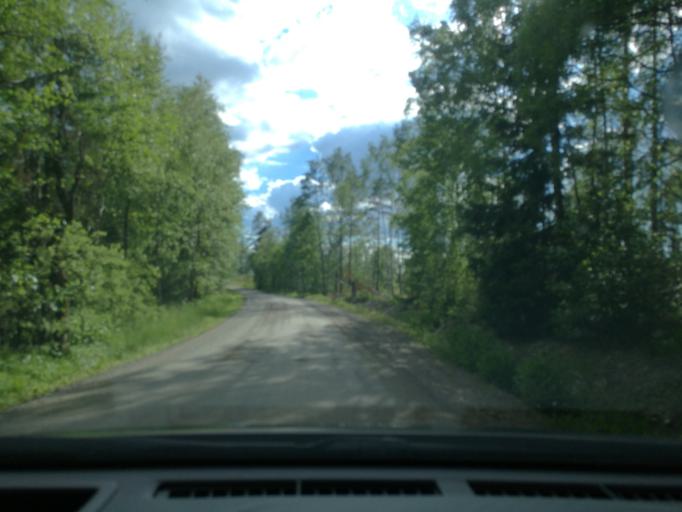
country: SE
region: Vaestmanland
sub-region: Surahammars Kommun
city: Ramnas
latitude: 59.8043
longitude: 16.2242
